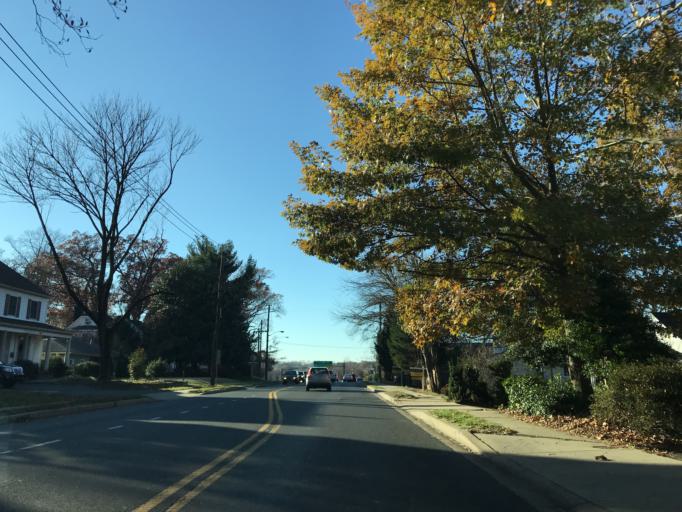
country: US
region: Maryland
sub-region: Montgomery County
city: Rockville
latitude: 39.0856
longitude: -77.1679
